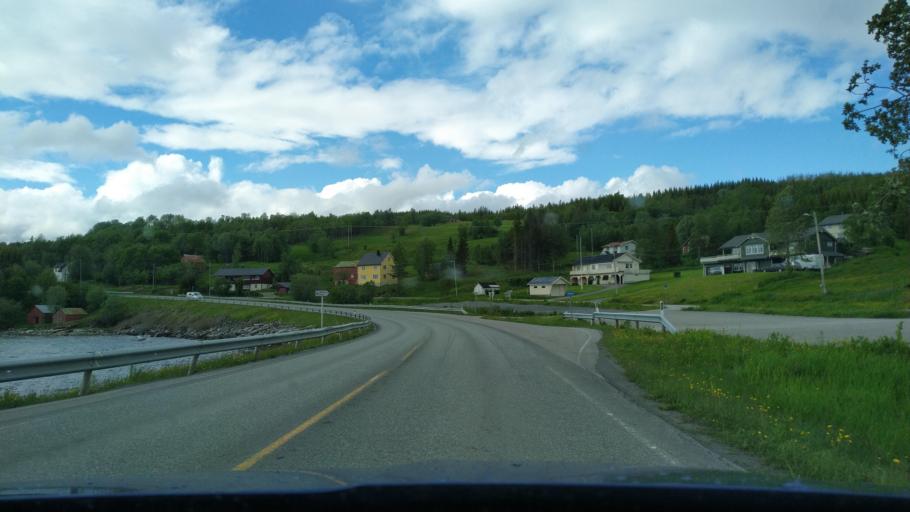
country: NO
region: Troms
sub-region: Sorreisa
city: Sorreisa
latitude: 69.1756
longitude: 18.0827
